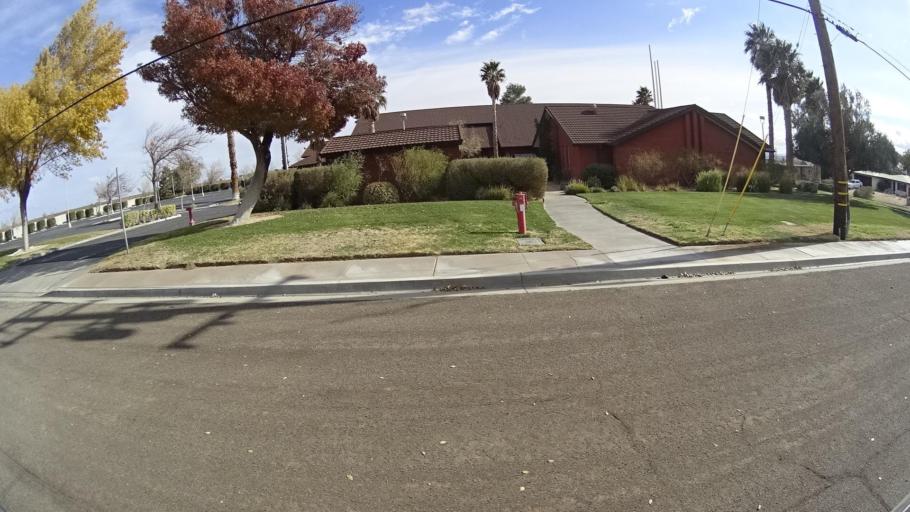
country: US
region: California
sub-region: Kern County
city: Mojave
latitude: 35.0631
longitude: -118.1947
